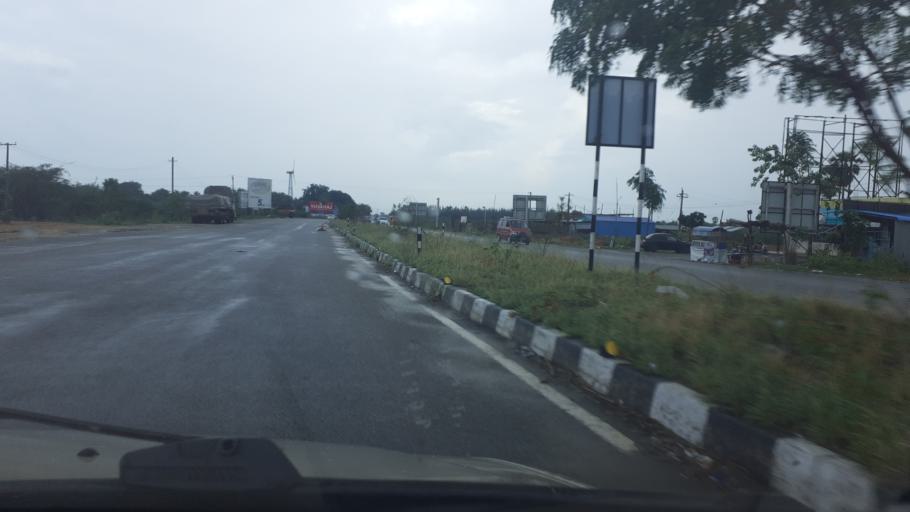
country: IN
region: Tamil Nadu
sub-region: Thoothukkudi
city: Kayattar
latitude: 8.9745
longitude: 77.7746
